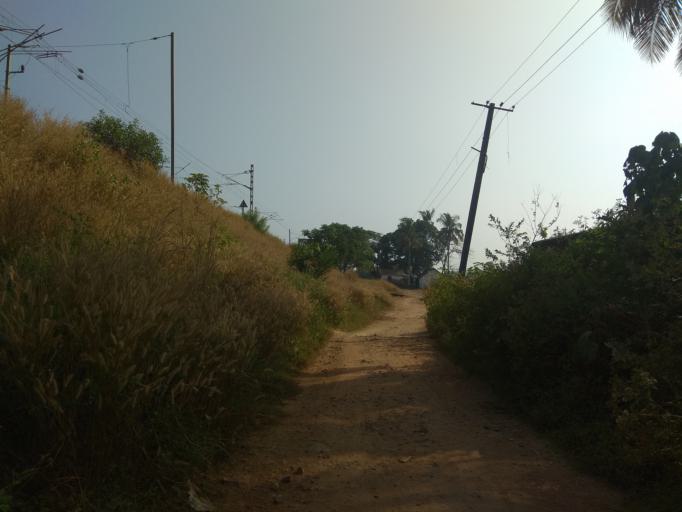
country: IN
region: Karnataka
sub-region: Dakshina Kannada
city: Ullal
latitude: 12.8446
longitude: 74.8560
